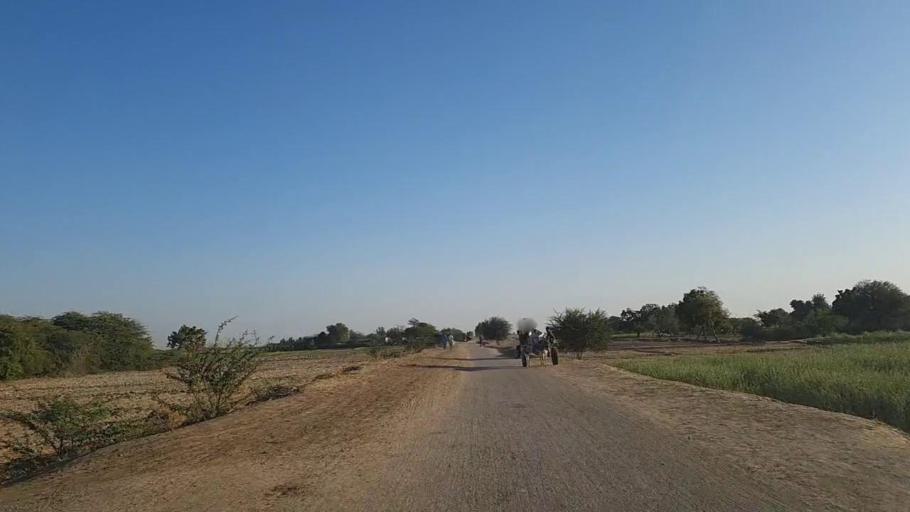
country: PK
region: Sindh
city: Naukot
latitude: 24.9921
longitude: 69.4017
